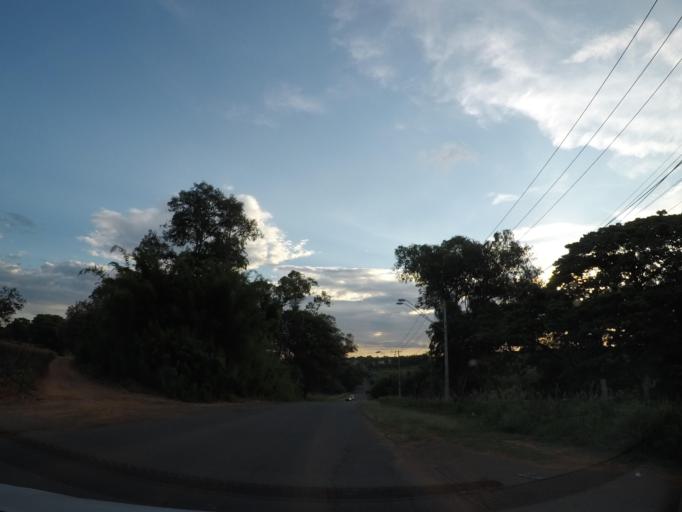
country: BR
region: Sao Paulo
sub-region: Sumare
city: Sumare
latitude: -22.8509
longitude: -47.2844
